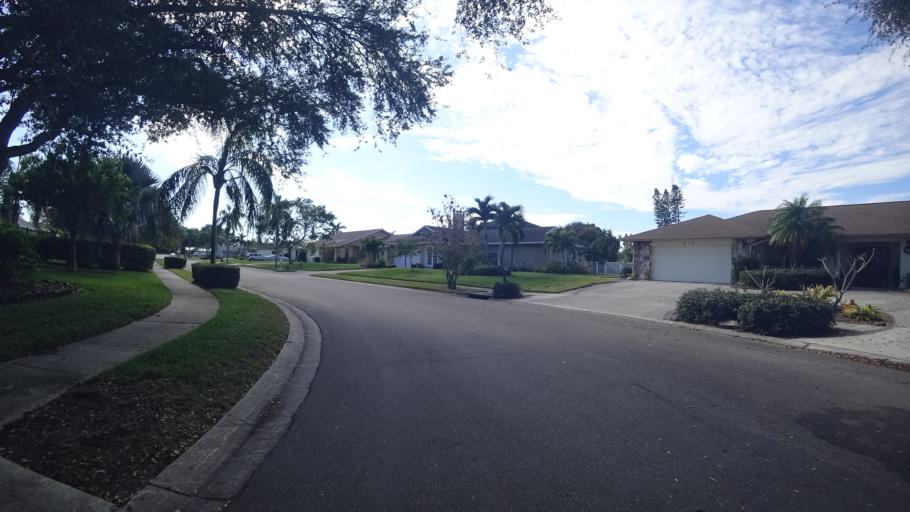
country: US
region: Florida
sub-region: Manatee County
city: West Bradenton
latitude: 27.5027
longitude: -82.6257
